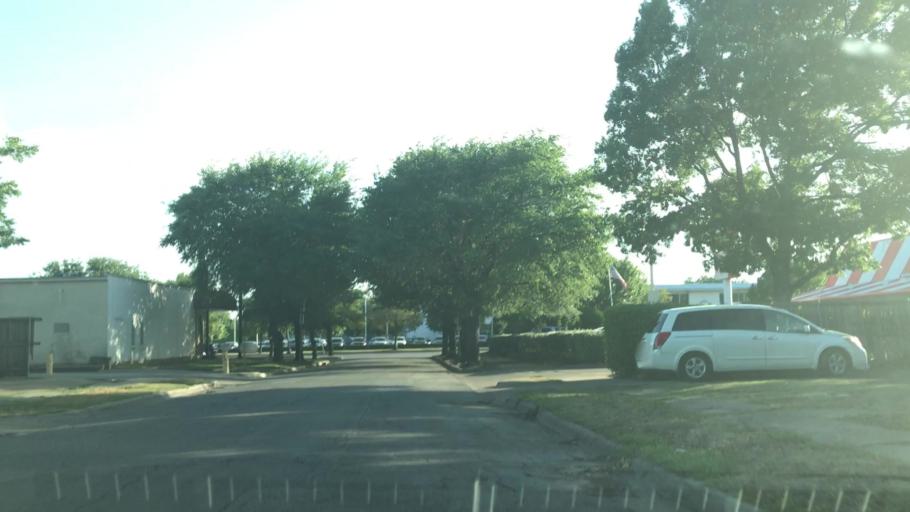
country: US
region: Texas
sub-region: Dallas County
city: University Park
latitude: 32.8289
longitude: -96.8237
